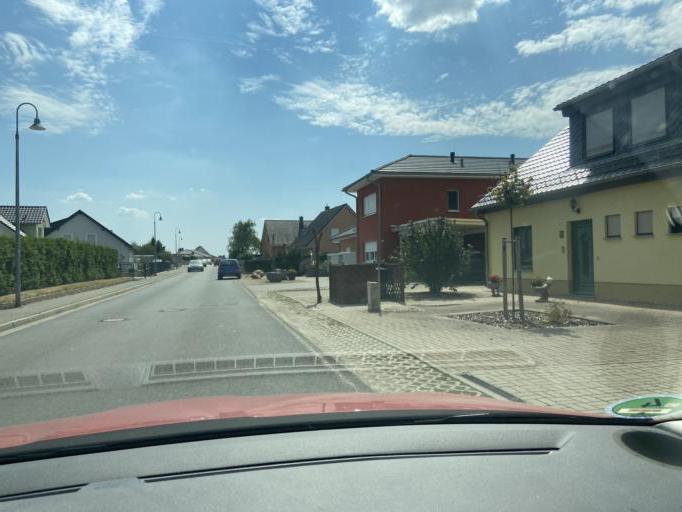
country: DE
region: Saxony
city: Tharandt
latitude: 51.0313
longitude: 13.5832
